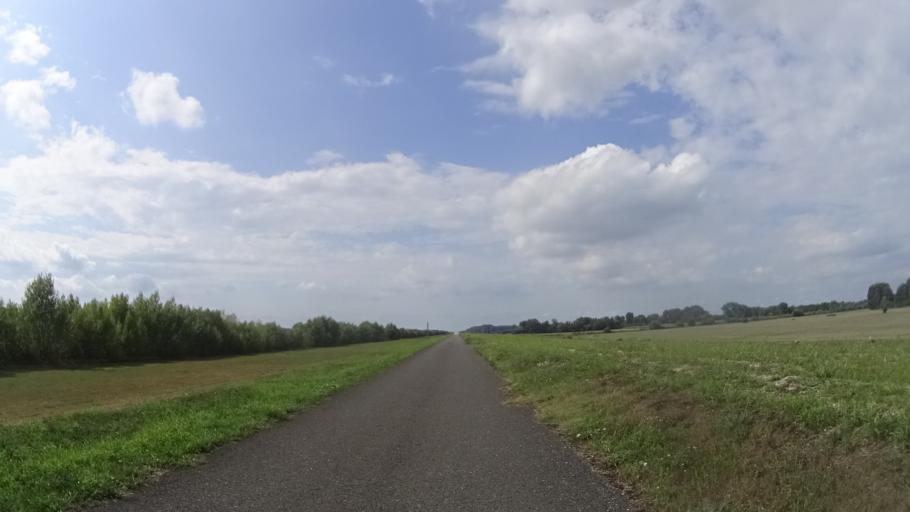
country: SK
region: Trnavsky
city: Gabcikovo
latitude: 47.8297
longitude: 17.6022
